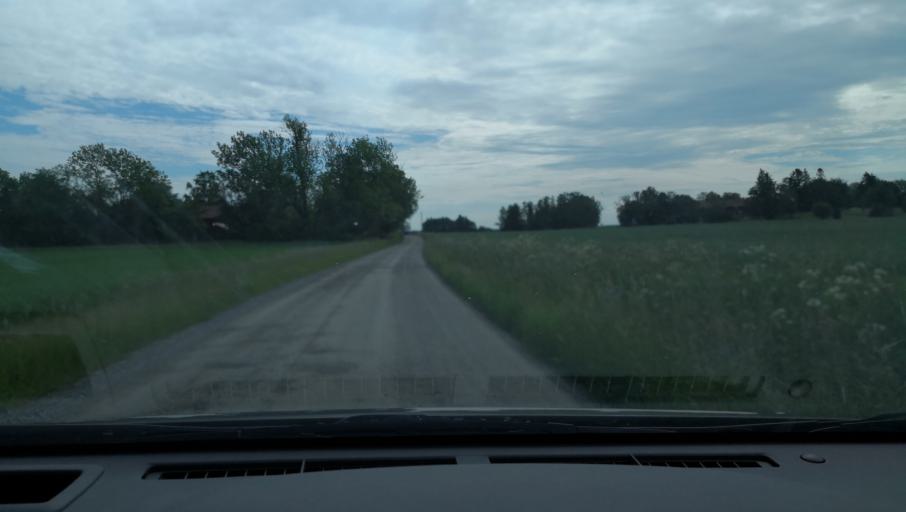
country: SE
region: Uppsala
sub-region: Enkopings Kommun
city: Enkoping
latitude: 59.7043
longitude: 17.1535
